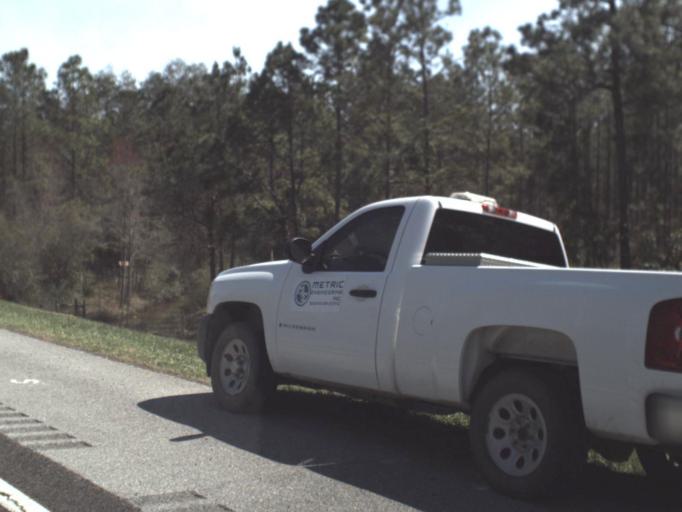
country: US
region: Florida
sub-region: Holmes County
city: Bonifay
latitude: 30.7607
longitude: -85.6520
